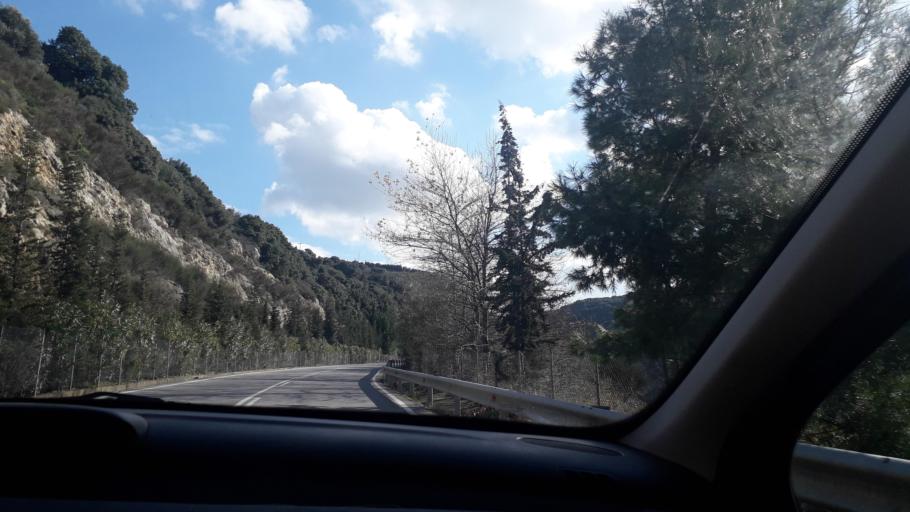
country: GR
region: Crete
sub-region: Nomos Rethymnis
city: Rethymno
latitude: 35.3329
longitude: 24.5274
